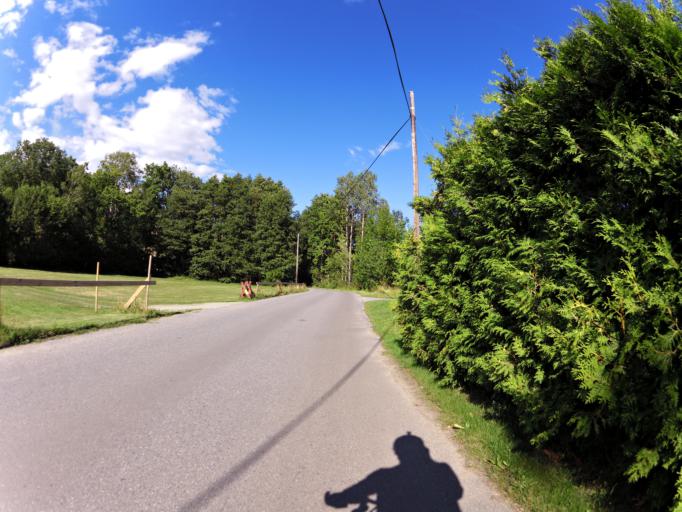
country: NO
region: Ostfold
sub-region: Fredrikstad
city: Fredrikstad
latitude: 59.1721
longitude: 10.8351
